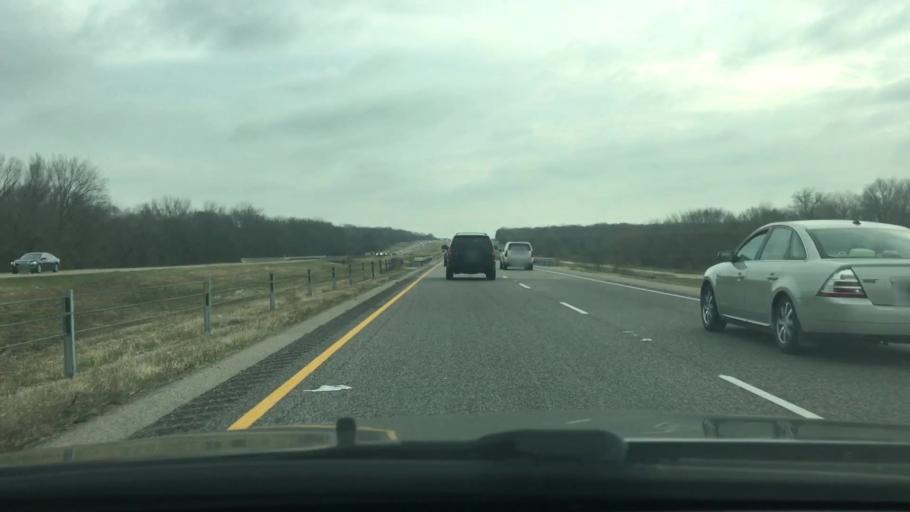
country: US
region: Texas
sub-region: Freestone County
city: Fairfield
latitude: 31.6511
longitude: -96.1603
